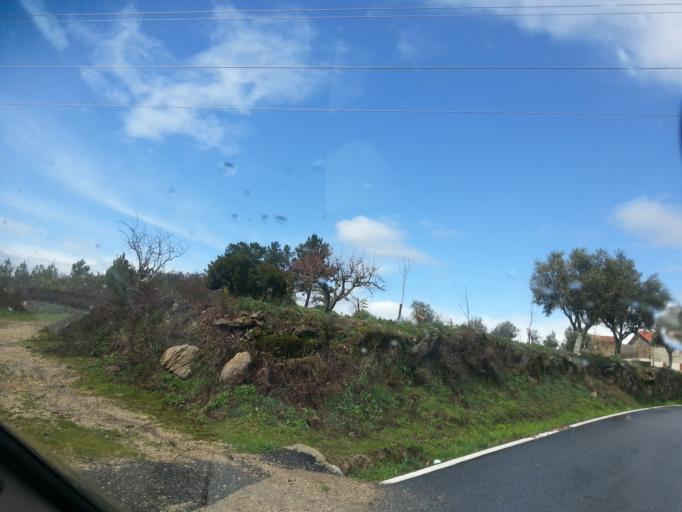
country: PT
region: Guarda
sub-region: Fornos de Algodres
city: Fornos de Algodres
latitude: 40.5758
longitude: -7.4693
